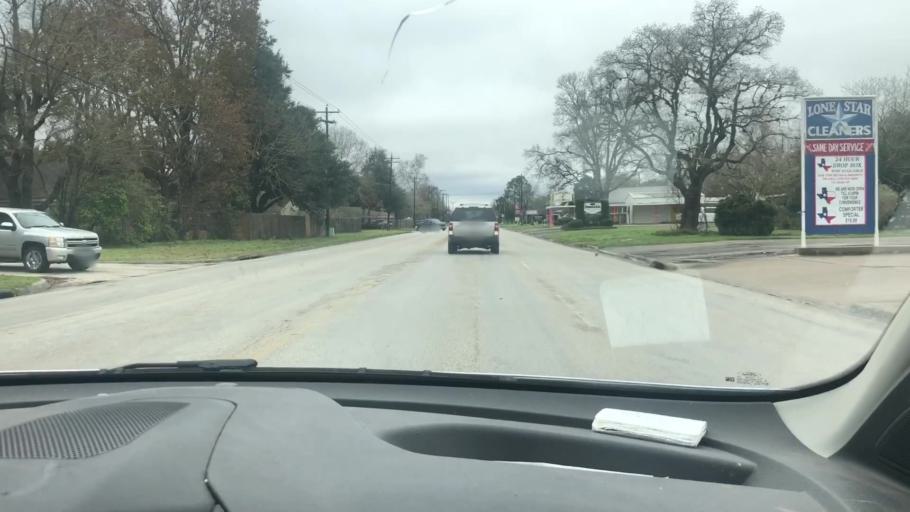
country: US
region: Texas
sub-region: Wharton County
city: Wharton
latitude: 29.3185
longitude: -96.0861
